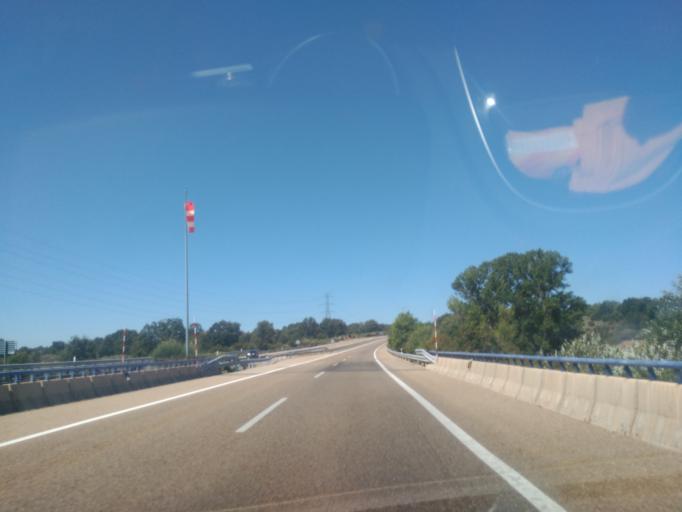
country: ES
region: Castille and Leon
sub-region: Provincia de Zamora
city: Mombuey
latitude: 42.0178
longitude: -6.3320
